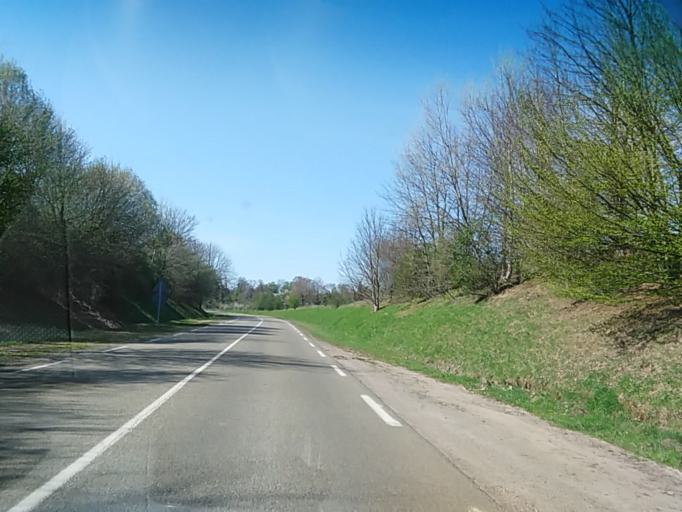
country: FR
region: Lower Normandy
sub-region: Departement de l'Orne
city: Damigny
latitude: 48.4487
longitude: 0.0505
